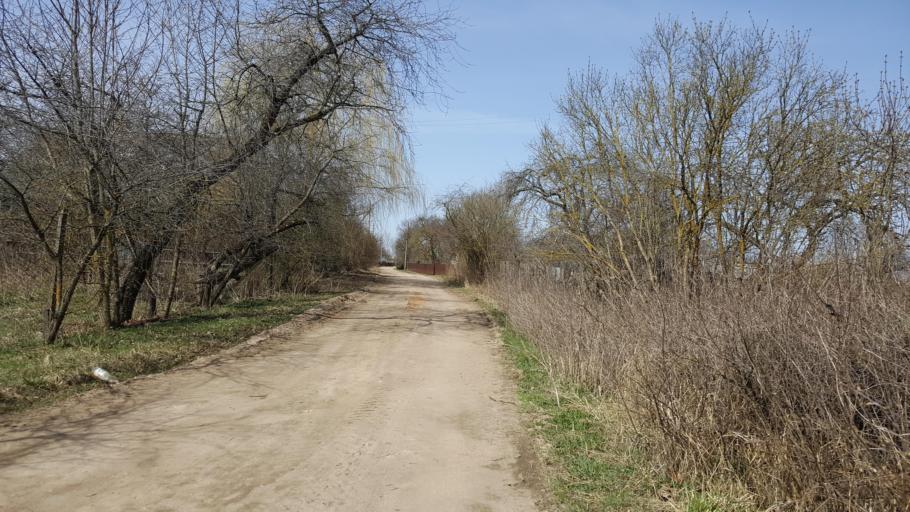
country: BY
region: Brest
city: Kamyanyets
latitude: 52.4630
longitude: 23.7244
